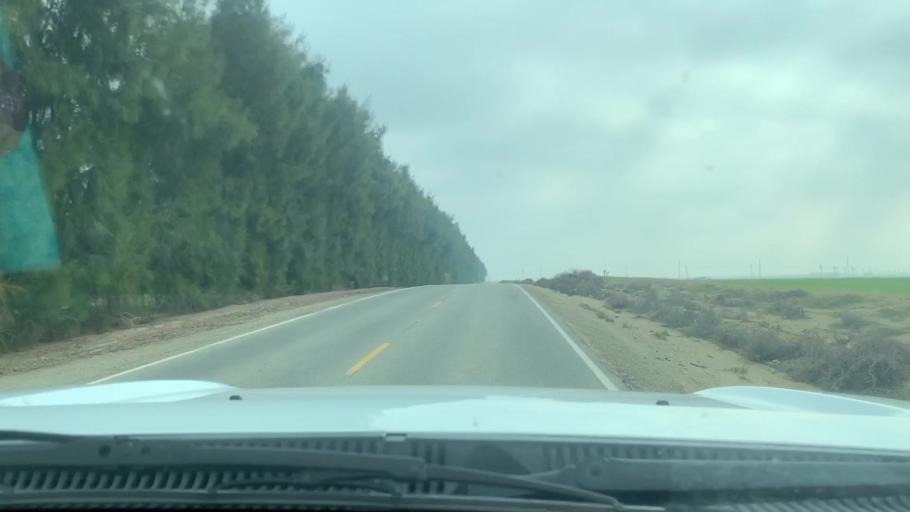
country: US
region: California
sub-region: Kern County
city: Lost Hills
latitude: 35.5060
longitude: -119.7447
